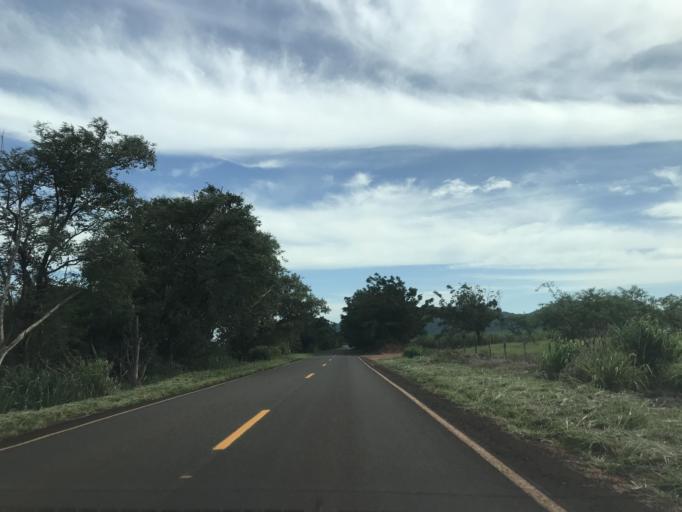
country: BR
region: Parana
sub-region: Paranavai
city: Nova Aurora
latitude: -22.8147
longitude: -52.6546
